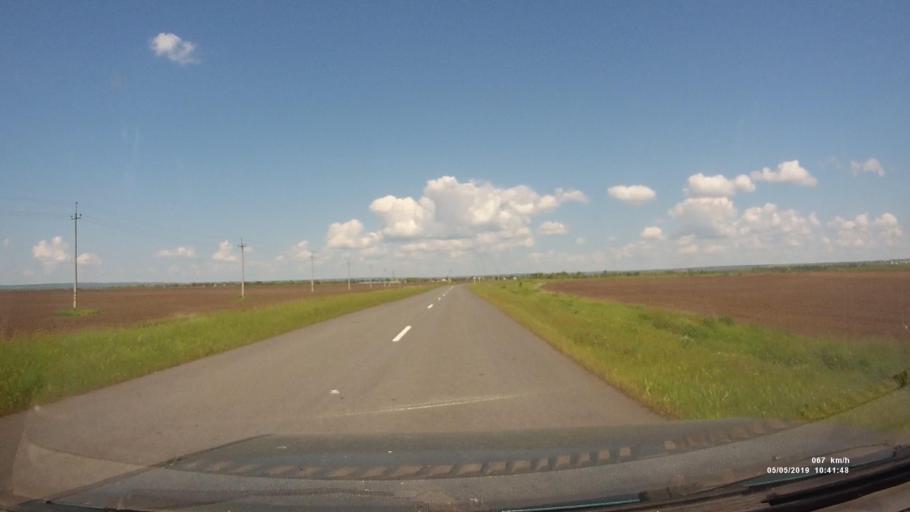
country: RU
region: Rostov
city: Ust'-Donetskiy
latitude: 47.5937
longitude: 40.8390
